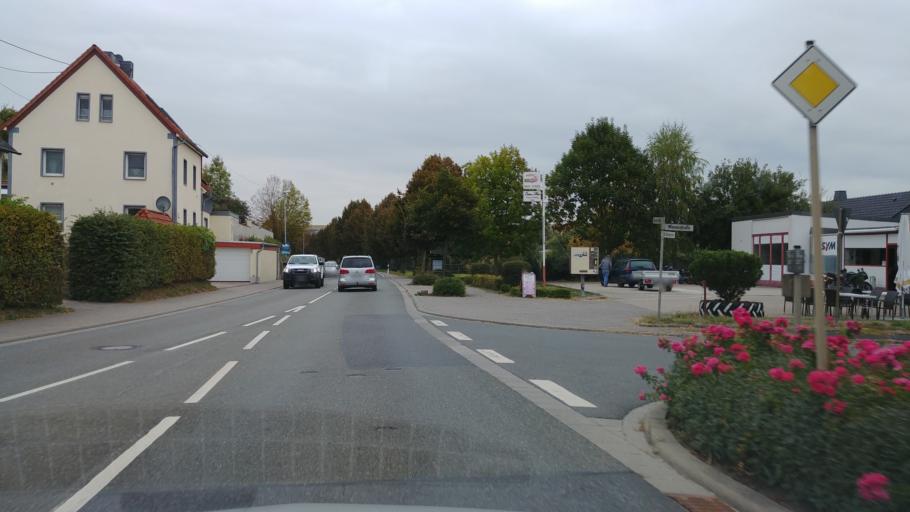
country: DE
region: Rheinland-Pfalz
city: Holzheim
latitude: 50.3474
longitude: 8.0478
